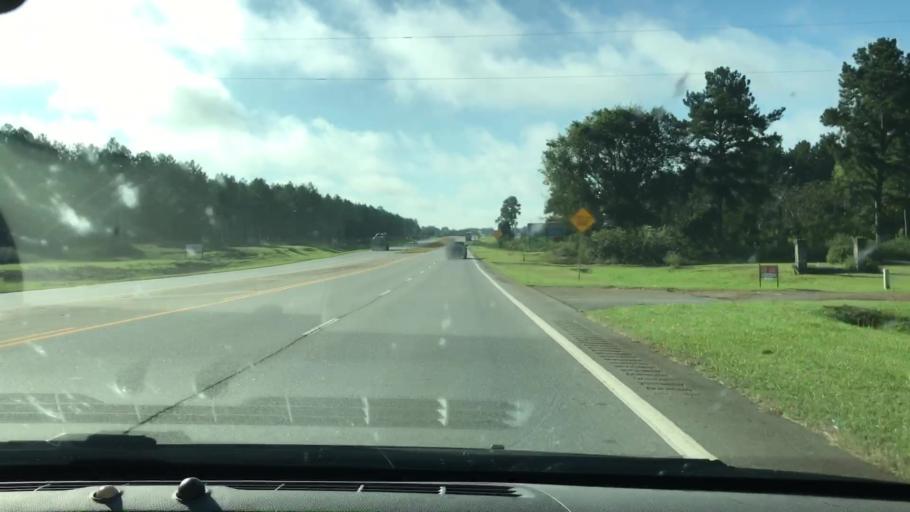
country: US
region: Georgia
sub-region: Terrell County
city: Dawson
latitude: 31.7516
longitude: -84.4225
